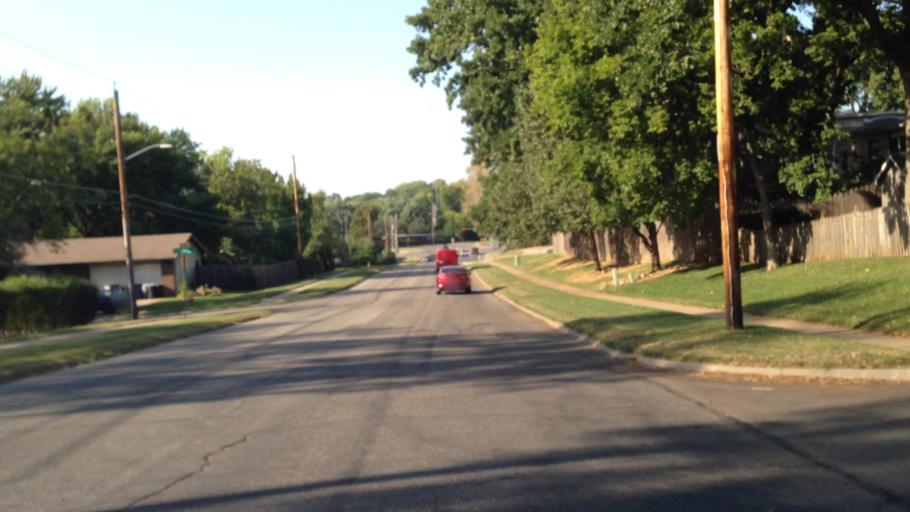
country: US
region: Kansas
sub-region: Douglas County
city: Lawrence
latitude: 38.9398
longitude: -95.2698
